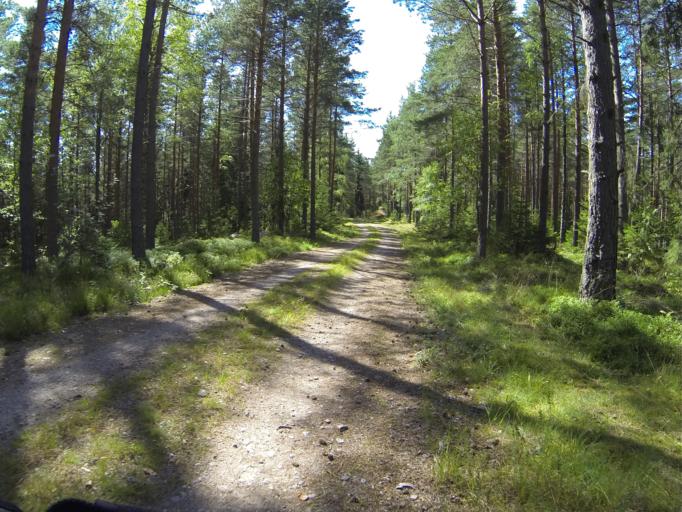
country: FI
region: Varsinais-Suomi
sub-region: Salo
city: Pernioe
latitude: 60.2838
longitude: 23.0658
